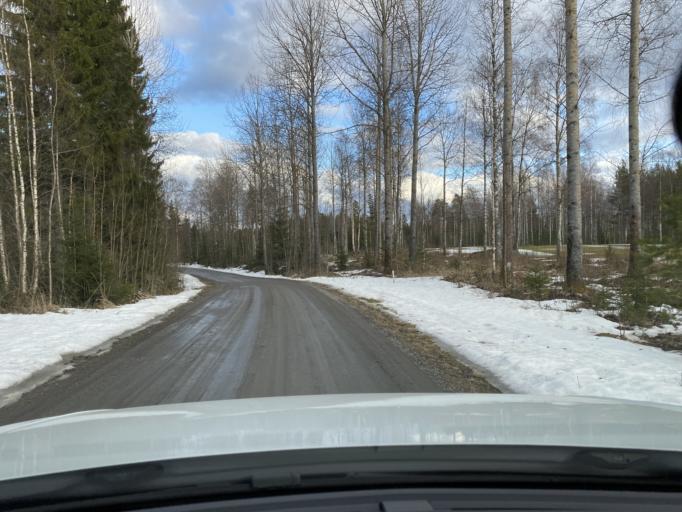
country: FI
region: Pirkanmaa
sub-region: Lounais-Pirkanmaa
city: Mouhijaervi
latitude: 61.4297
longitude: 22.9952
